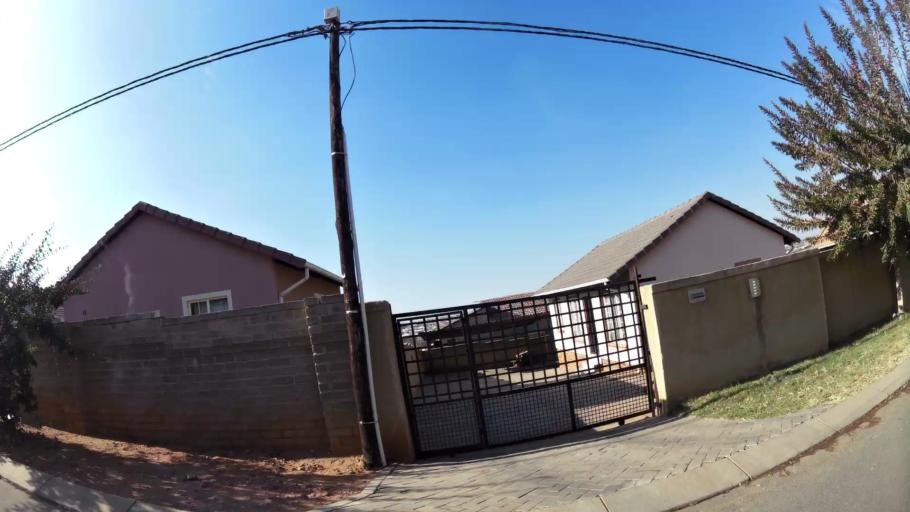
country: ZA
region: Gauteng
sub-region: West Rand District Municipality
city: Muldersdriseloop
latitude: -26.0315
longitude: 27.9164
